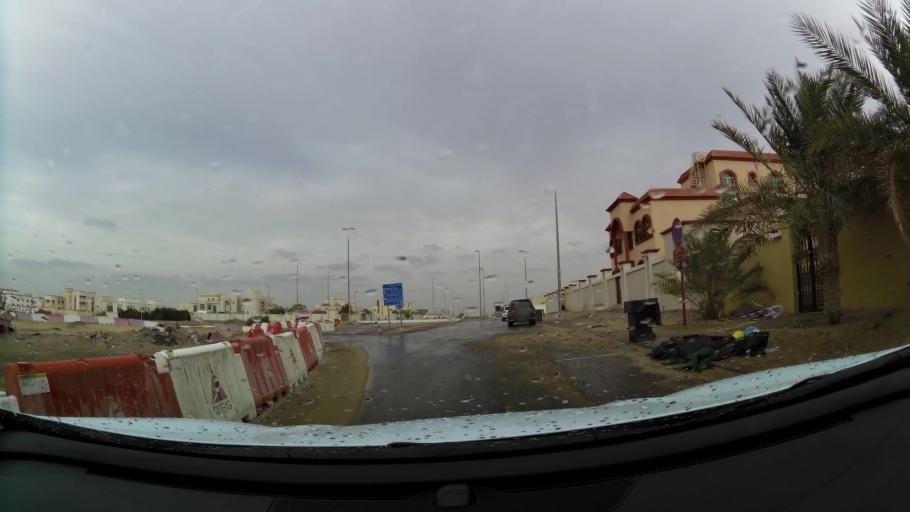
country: AE
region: Abu Dhabi
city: Abu Dhabi
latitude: 24.3556
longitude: 54.6274
